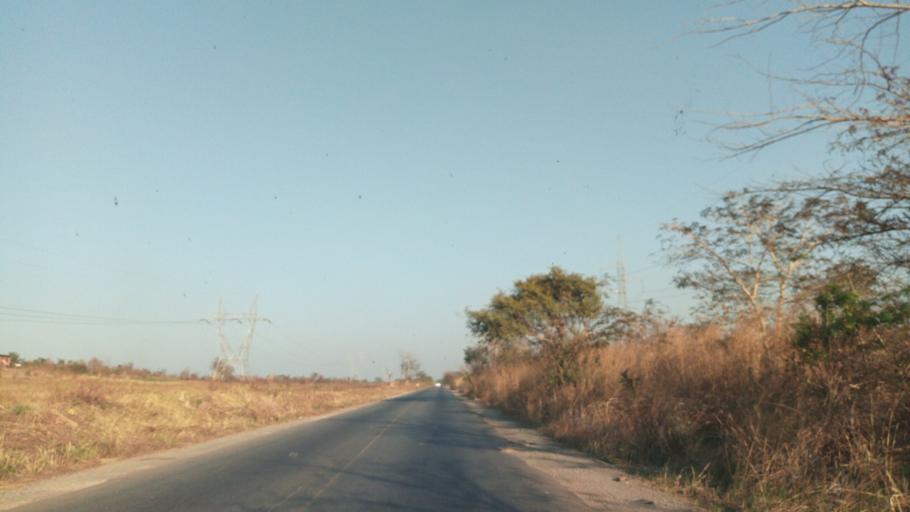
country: CD
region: Katanga
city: Likasi
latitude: -11.1072
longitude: 27.0193
